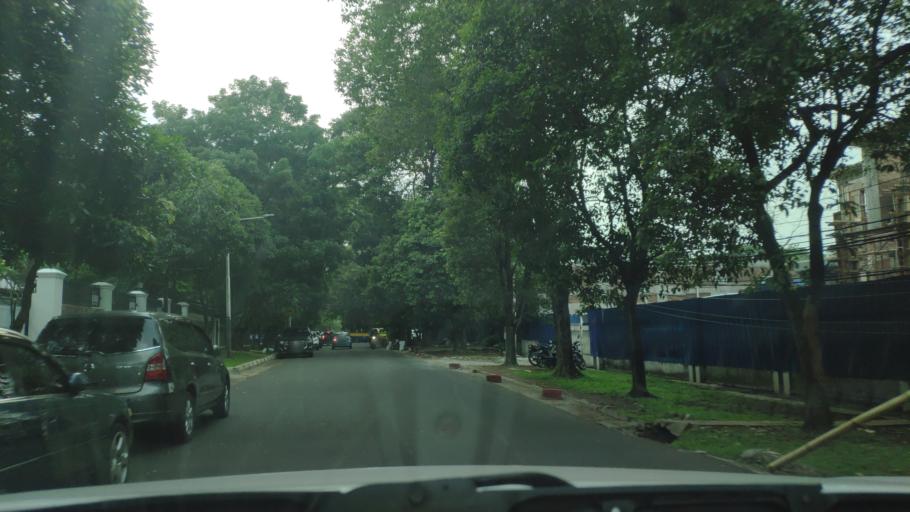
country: ID
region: Jakarta Raya
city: Jakarta
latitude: -6.2356
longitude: 106.8041
